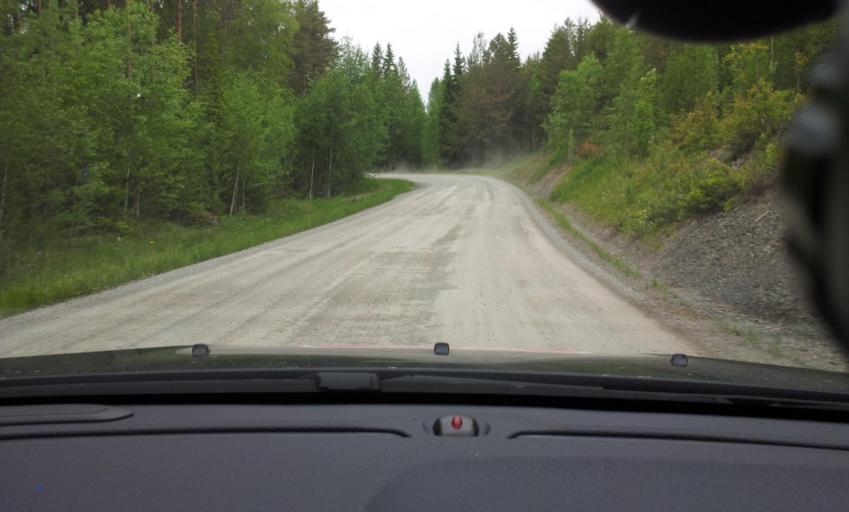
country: SE
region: Jaemtland
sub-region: OEstersunds Kommun
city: Ostersund
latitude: 62.9787
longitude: 14.6433
